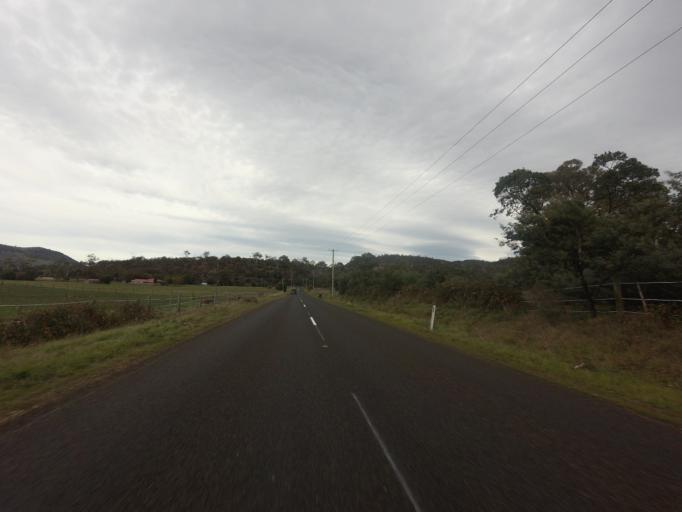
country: AU
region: Tasmania
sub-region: Brighton
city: Bridgewater
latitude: -42.6746
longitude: 147.1543
